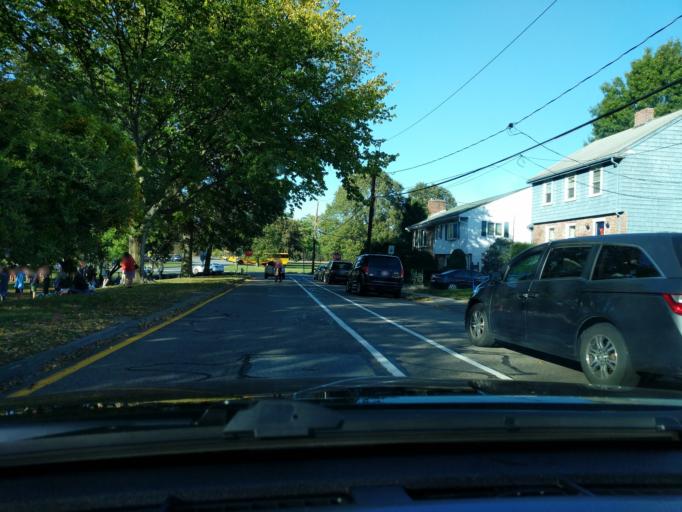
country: US
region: Massachusetts
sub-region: Middlesex County
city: Belmont
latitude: 42.3939
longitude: -71.1620
